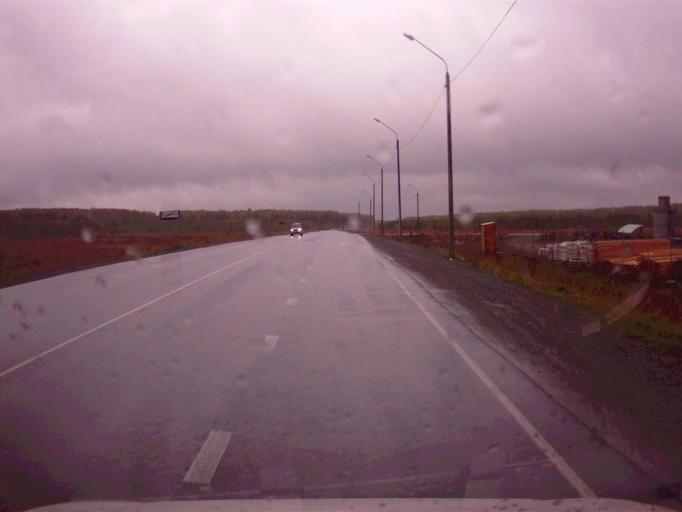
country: RU
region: Chelyabinsk
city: Tayginka
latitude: 55.5013
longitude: 60.6365
